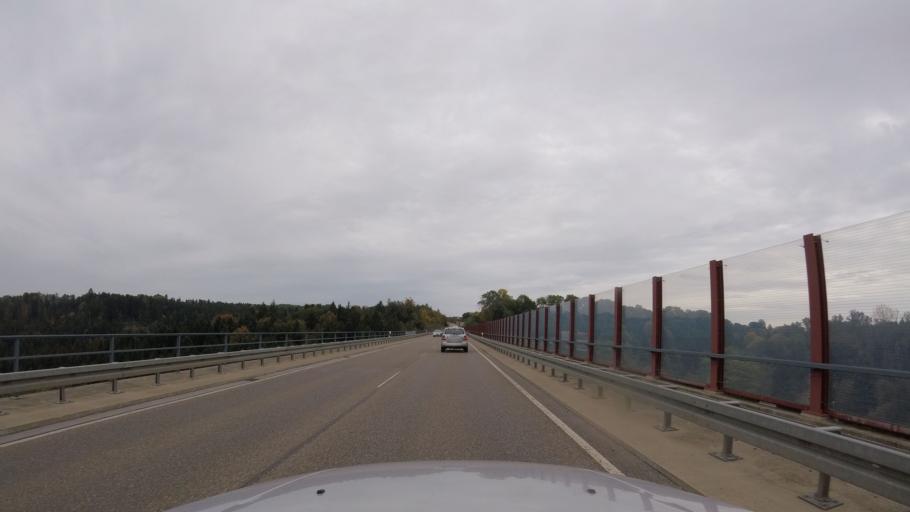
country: DE
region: Baden-Wuerttemberg
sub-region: Regierungsbezirk Stuttgart
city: Mutlangen
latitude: 48.8256
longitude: 9.7854
